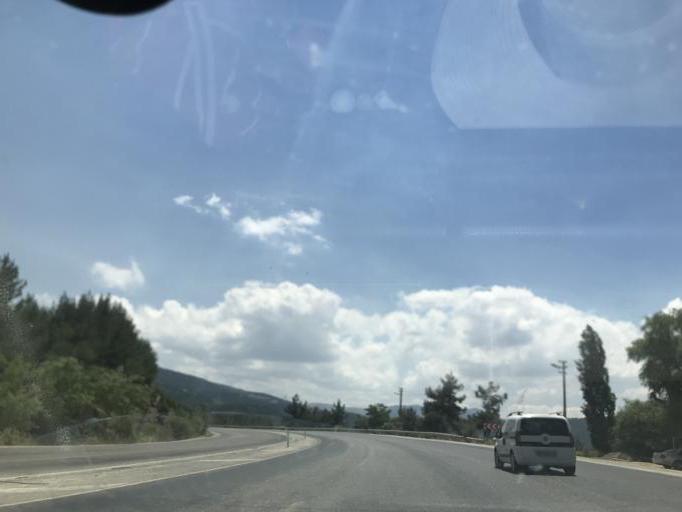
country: TR
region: Denizli
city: Honaz
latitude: 37.6786
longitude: 29.2238
